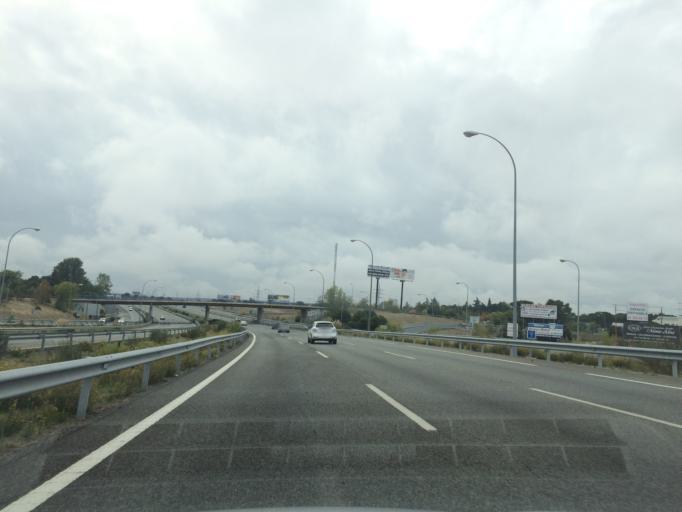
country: ES
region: Madrid
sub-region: Provincia de Madrid
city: Pozuelo de Alarcon
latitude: 40.4270
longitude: -3.8361
